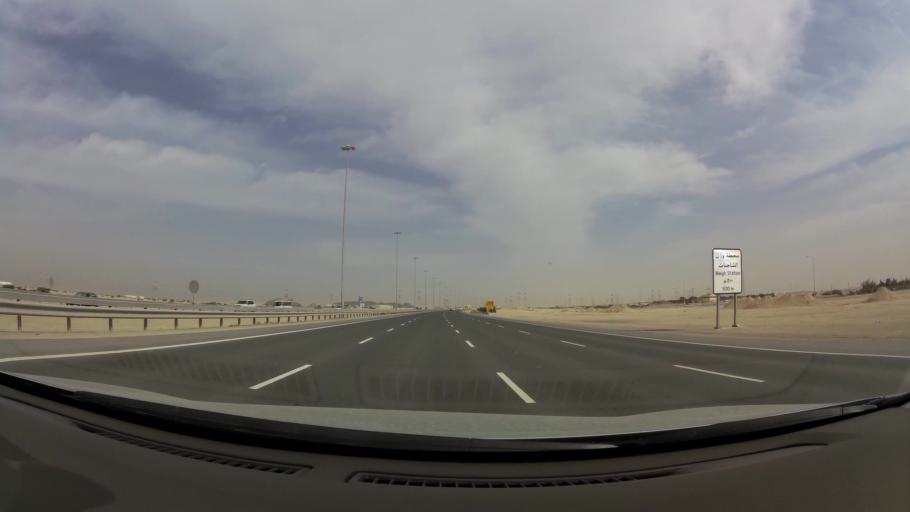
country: QA
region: Baladiyat ar Rayyan
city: Ash Shahaniyah
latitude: 25.3497
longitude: 51.2994
